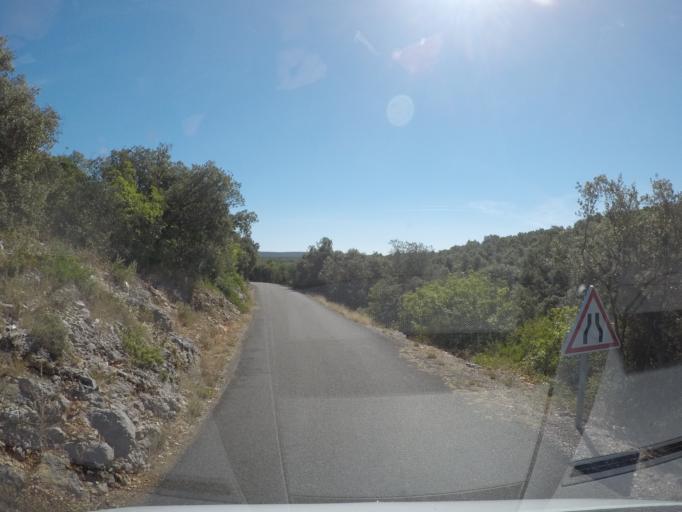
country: FR
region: Languedoc-Roussillon
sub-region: Departement de l'Herault
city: Vailhauques
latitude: 43.7137
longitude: 3.6813
